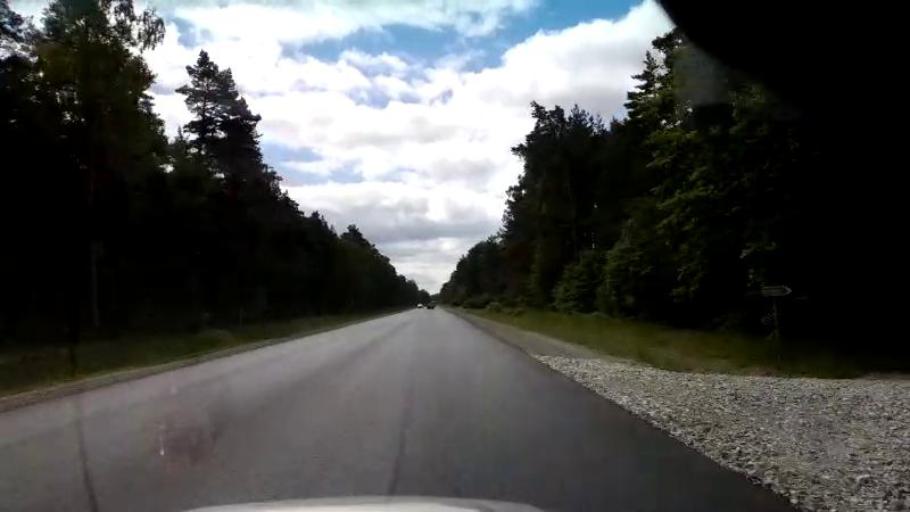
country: LV
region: Salacgrivas
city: Salacgriva
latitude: 57.8043
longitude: 24.3490
